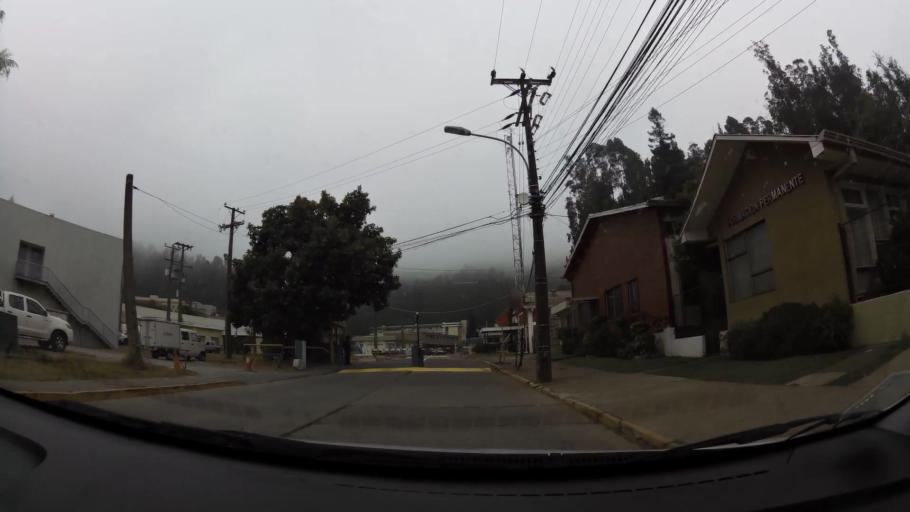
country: CL
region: Biobio
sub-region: Provincia de Concepcion
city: Concepcion
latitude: -36.8338
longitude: -73.0338
